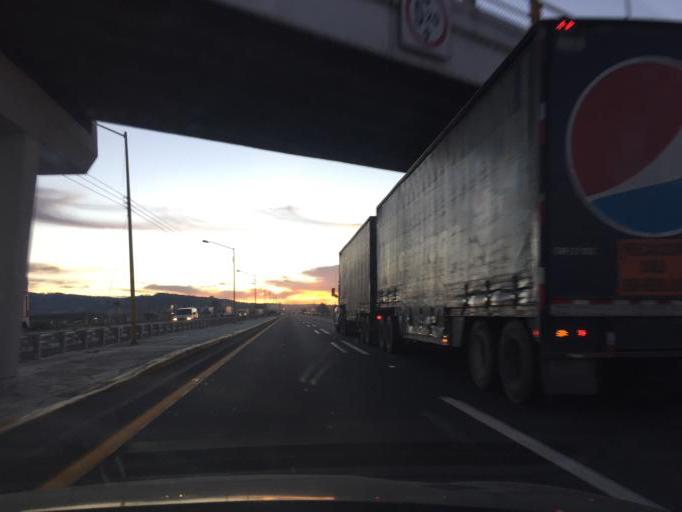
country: MX
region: Puebla
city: San Jose Esperanza
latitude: 18.8671
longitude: -97.3781
